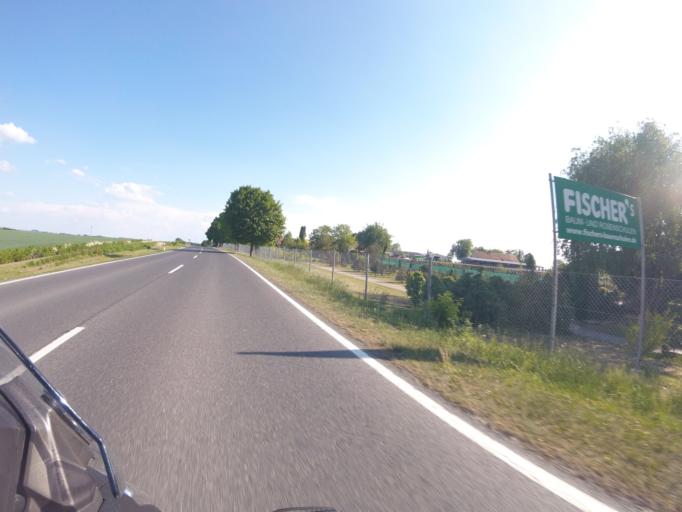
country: DE
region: Bavaria
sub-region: Upper Bavaria
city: Fahrenzhausen
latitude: 48.3637
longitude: 11.5491
